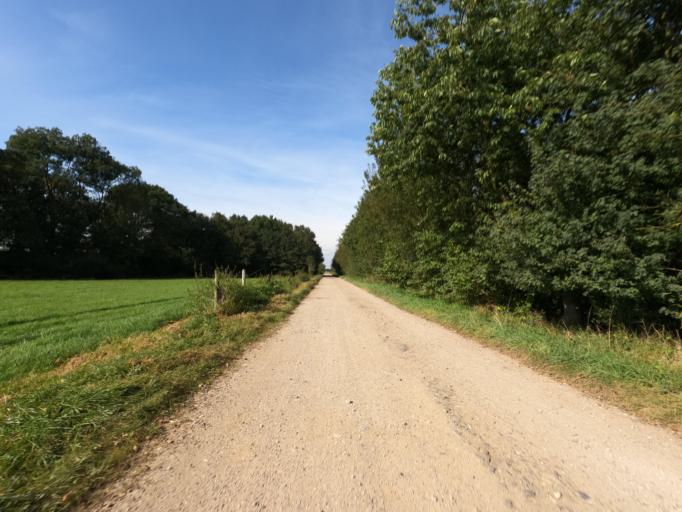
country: DE
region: North Rhine-Westphalia
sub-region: Regierungsbezirk Koln
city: Linnich
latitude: 50.9681
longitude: 6.2933
